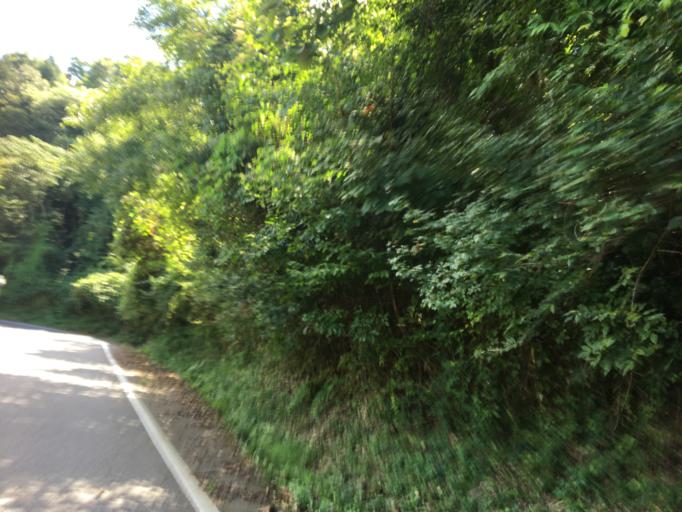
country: JP
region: Okayama
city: Tsuyama
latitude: 34.8973
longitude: 134.1321
